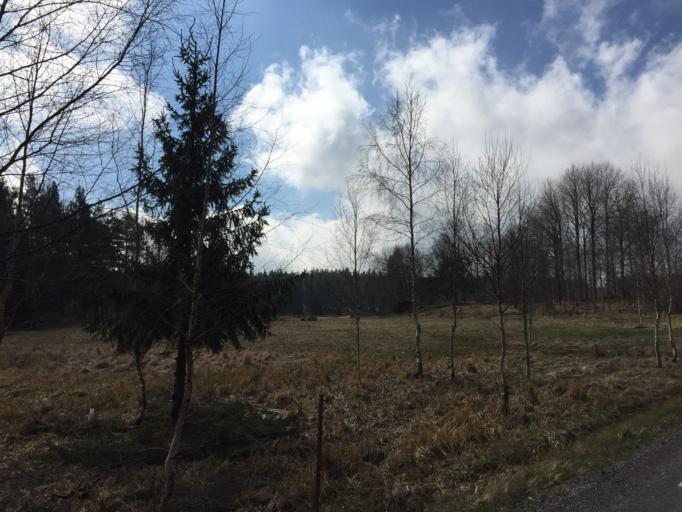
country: SE
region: Soedermanland
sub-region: Gnesta Kommun
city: Gnesta
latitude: 59.0205
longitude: 17.1827
